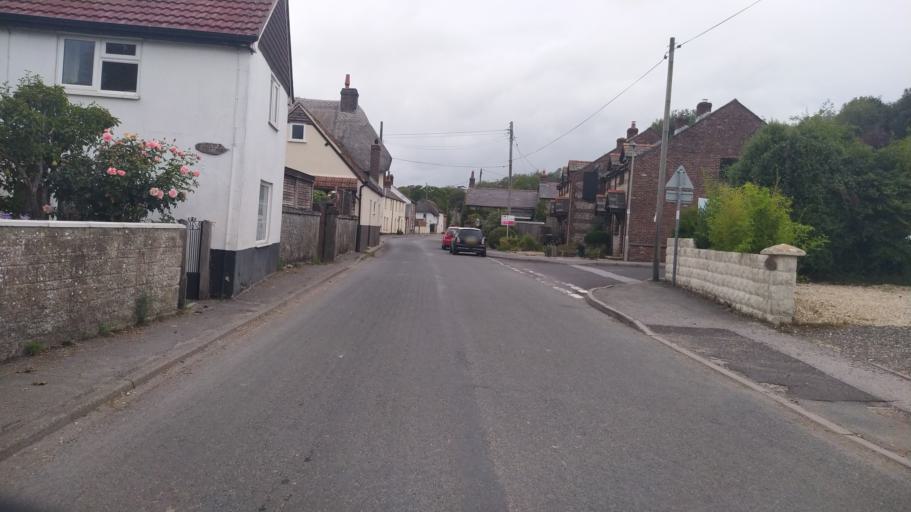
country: GB
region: England
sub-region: Dorset
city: Dorchester
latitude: 50.7945
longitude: -2.4173
